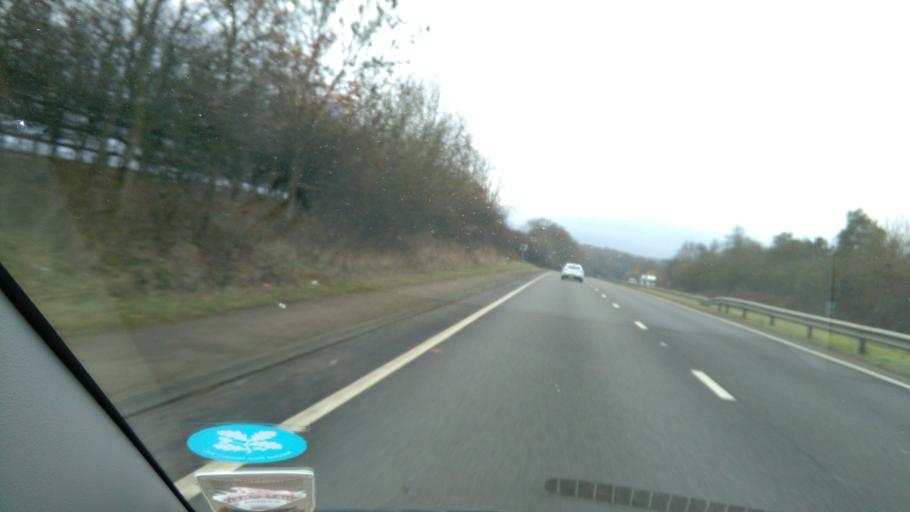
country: GB
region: England
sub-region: Northamptonshire
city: Blisworth
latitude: 52.1578
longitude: -0.9650
